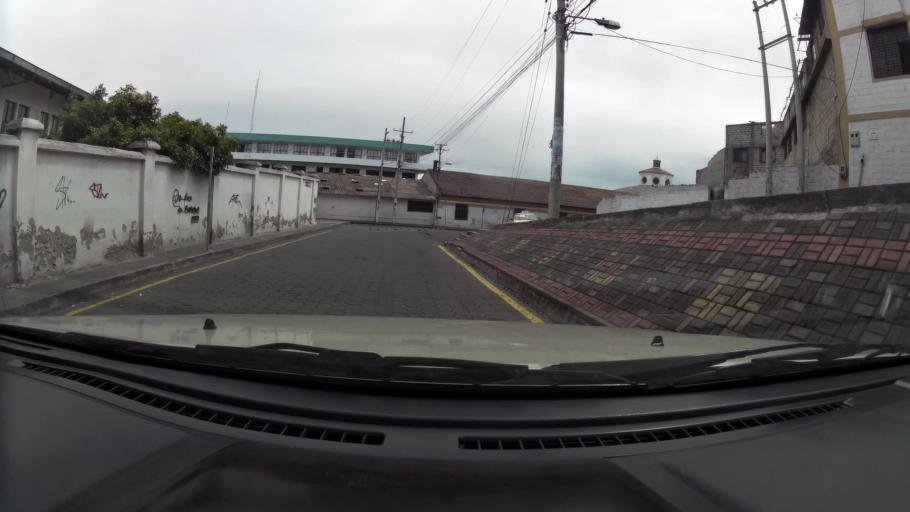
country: EC
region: Cotopaxi
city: Latacunga
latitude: -0.9293
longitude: -78.6179
